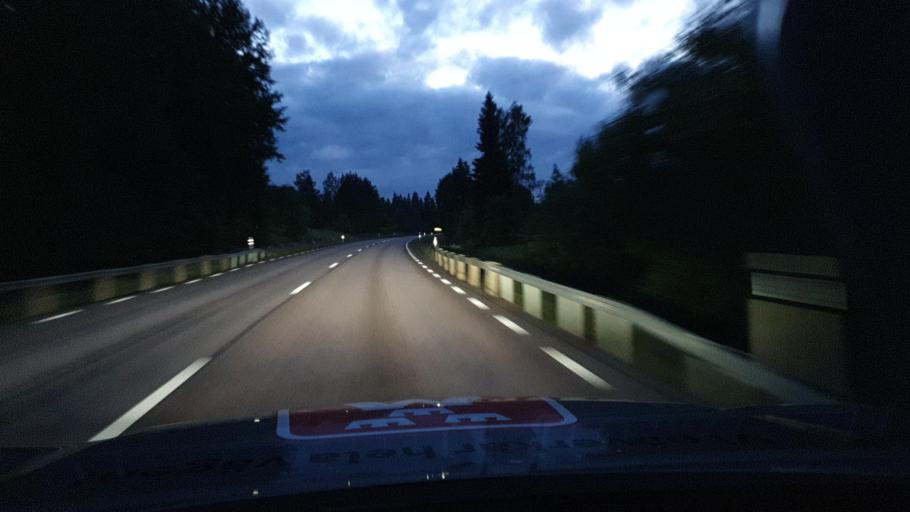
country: SE
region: Vaermland
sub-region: Storfors Kommun
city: Storfors
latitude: 59.4691
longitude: 14.3341
